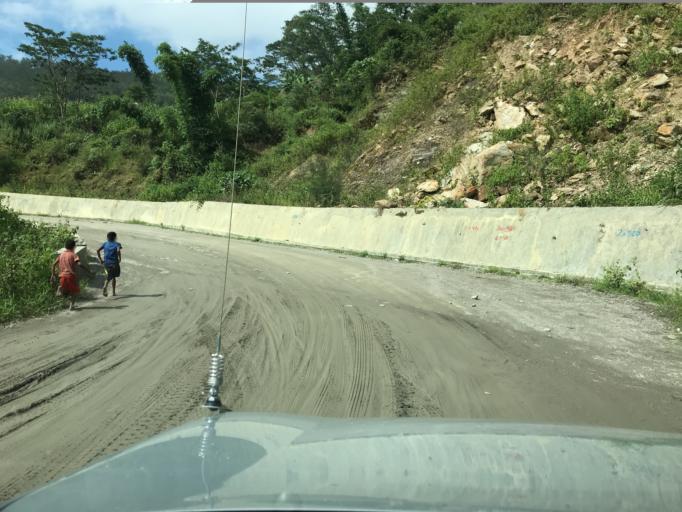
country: TL
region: Aileu
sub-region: Aileu Villa
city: Aileu
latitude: -8.6641
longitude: 125.5503
